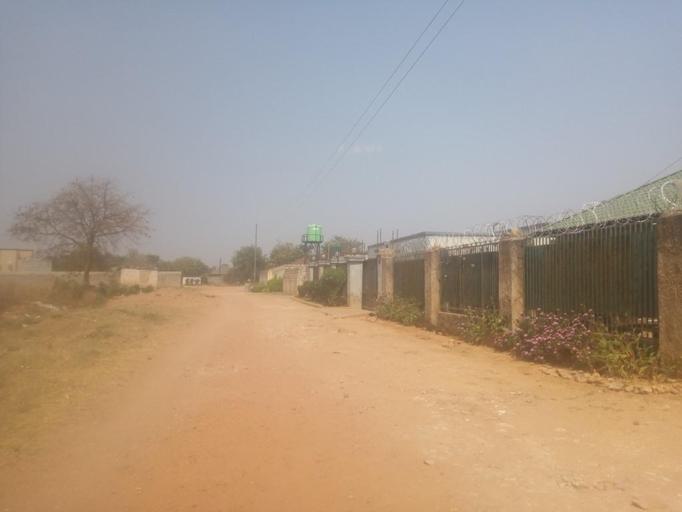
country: ZM
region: Lusaka
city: Lusaka
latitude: -15.3999
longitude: 28.3923
